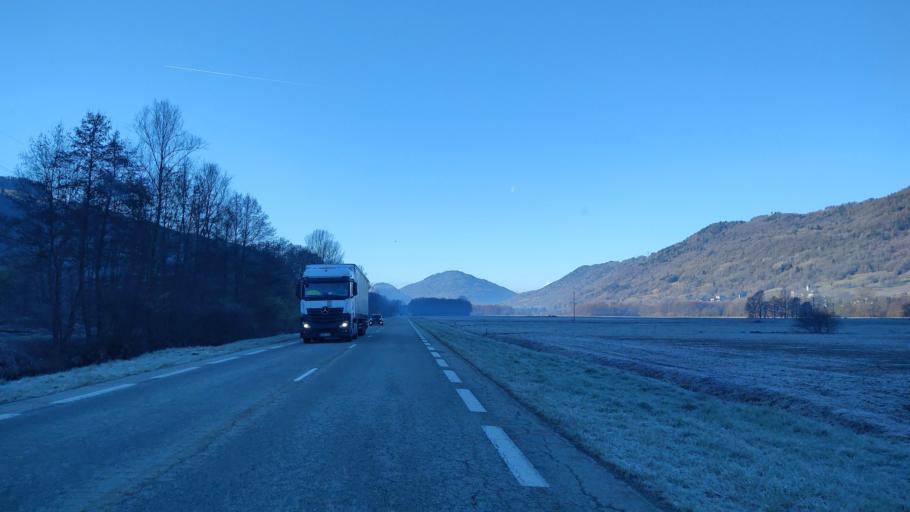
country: FR
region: Rhone-Alpes
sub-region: Departement de la Savoie
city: Coise-Saint-Jean-Pied-Gauthier
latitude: 45.5031
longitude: 6.1658
